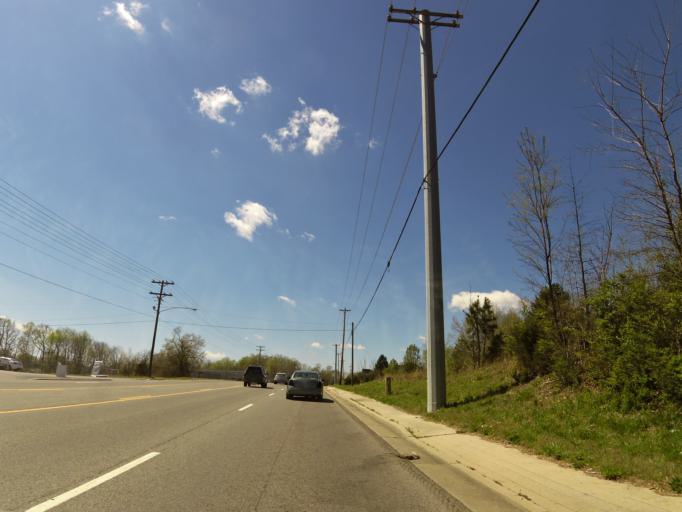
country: US
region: Tennessee
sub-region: DeKalb County
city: Smithville
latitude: 35.9587
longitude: -85.8305
